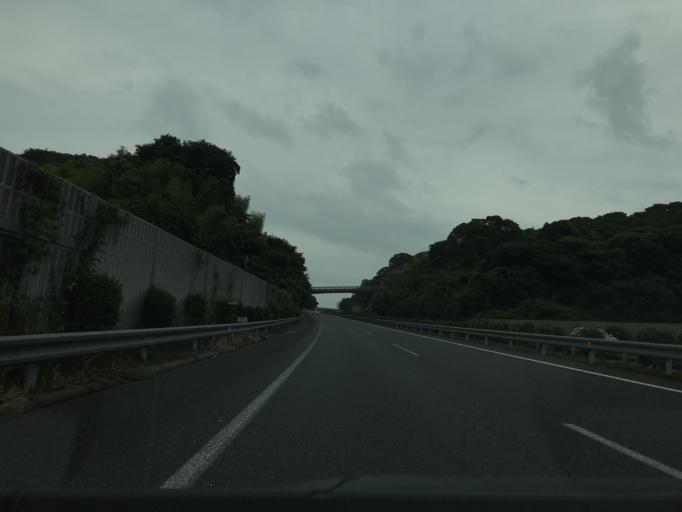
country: JP
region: Fukuoka
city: Kanda
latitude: 33.7998
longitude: 130.9540
